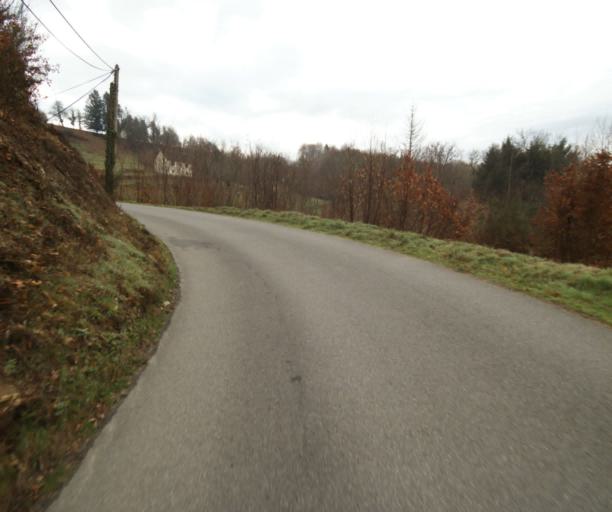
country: FR
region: Limousin
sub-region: Departement de la Correze
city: Chameyrat
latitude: 45.2332
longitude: 1.7310
